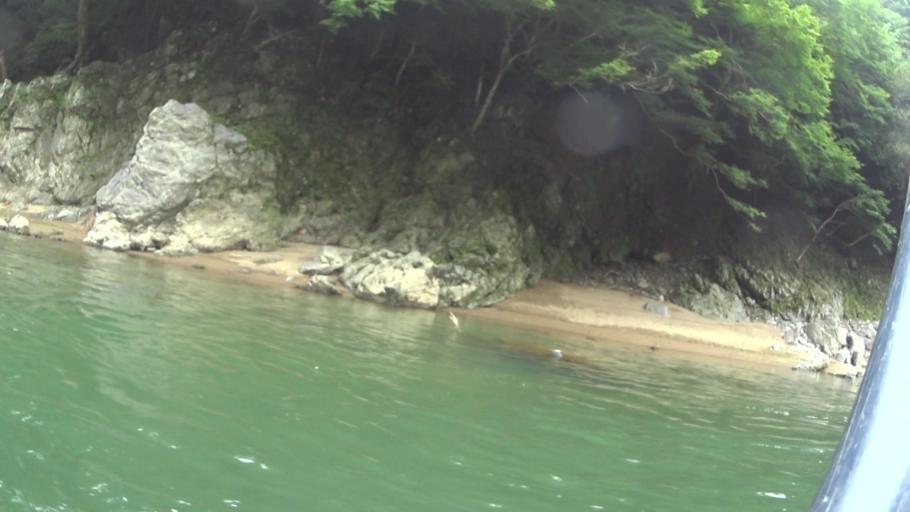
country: JP
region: Kyoto
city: Kameoka
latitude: 35.0207
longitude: 135.6262
